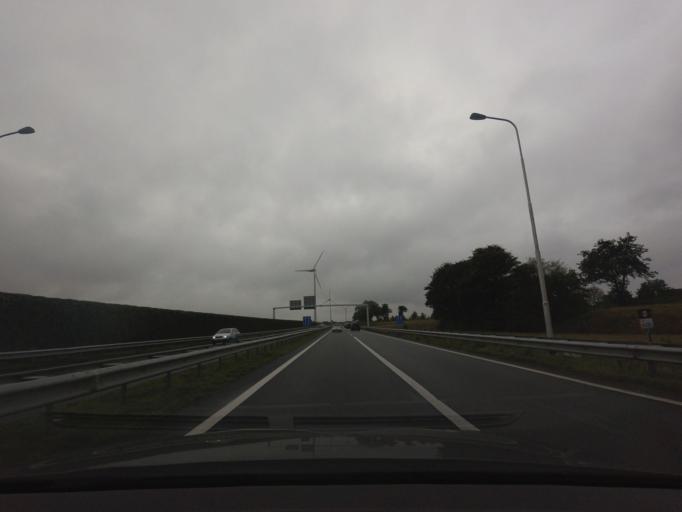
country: NL
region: North Holland
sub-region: Gemeente Langedijk
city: Broek op Langedijk
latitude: 52.6549
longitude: 4.8004
